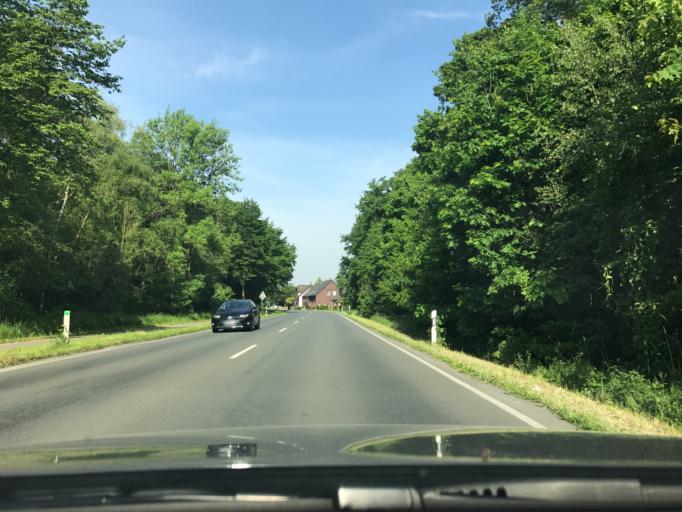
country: DE
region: North Rhine-Westphalia
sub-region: Regierungsbezirk Dusseldorf
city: Rheurdt
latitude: 51.4399
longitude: 6.4994
